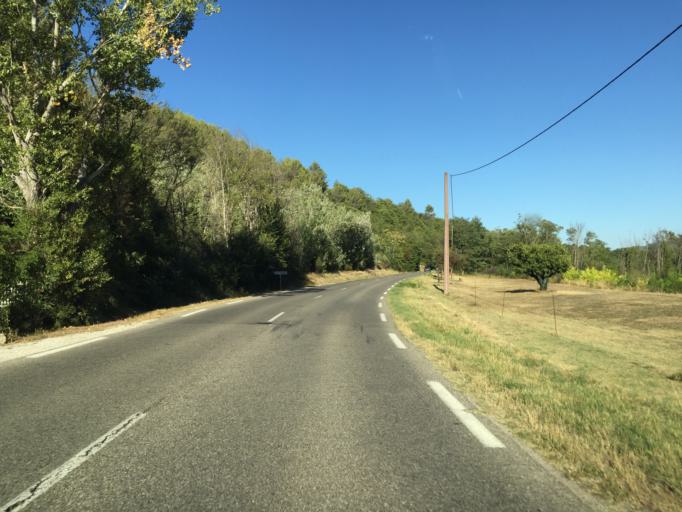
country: FR
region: Provence-Alpes-Cote d'Azur
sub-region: Departement des Alpes-de-Haute-Provence
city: Cereste
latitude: 43.8535
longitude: 5.5114
